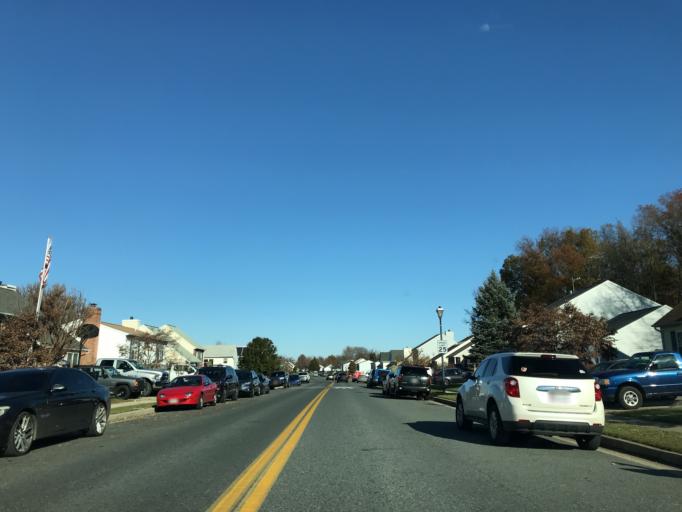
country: US
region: Maryland
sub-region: Baltimore County
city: Bowleys Quarters
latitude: 39.3653
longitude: -76.3587
